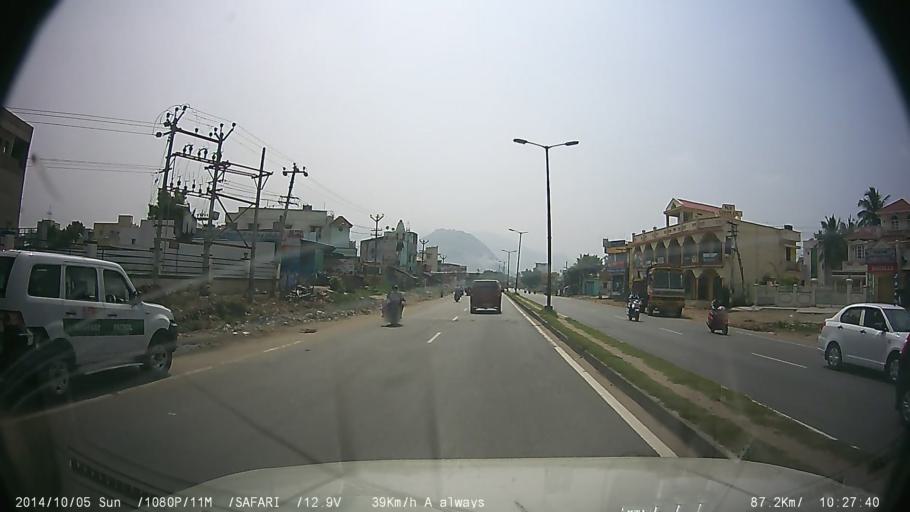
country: IN
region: Tamil Nadu
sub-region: Salem
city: Salem
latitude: 11.6327
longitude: 78.1276
